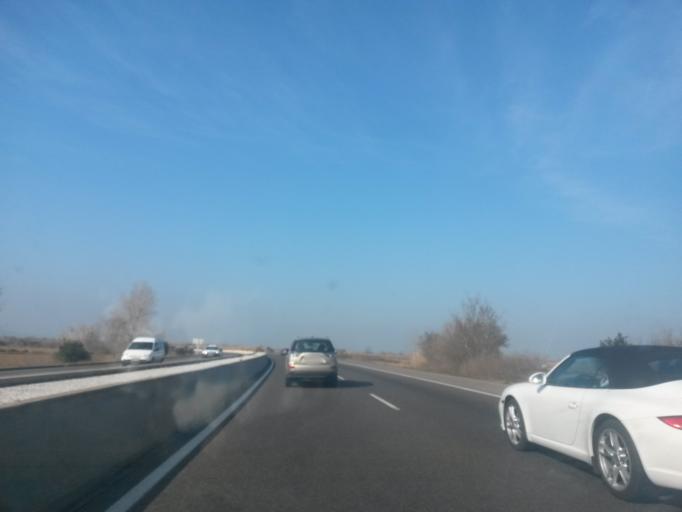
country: ES
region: Catalonia
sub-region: Provincia de Girona
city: Vila-sacra
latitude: 42.2641
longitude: 3.0346
